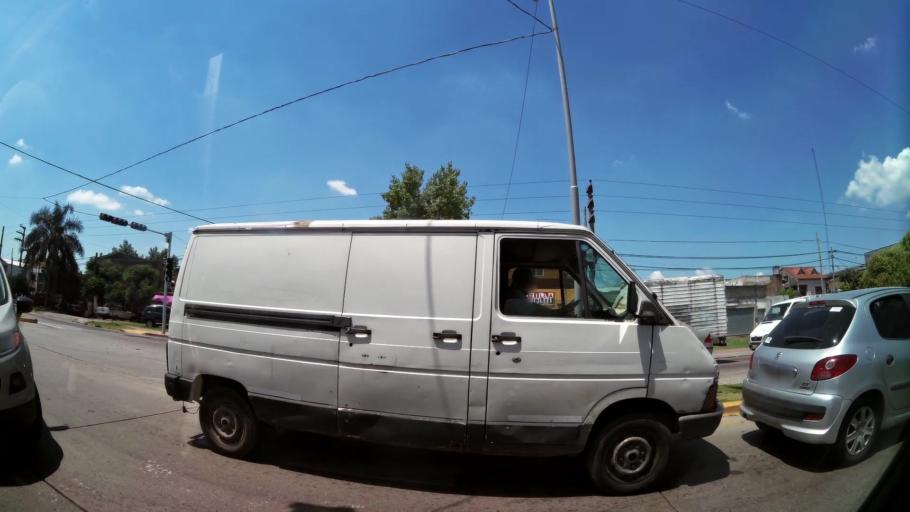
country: AR
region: Buenos Aires
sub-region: Partido de Tigre
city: Tigre
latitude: -34.4407
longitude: -58.5807
